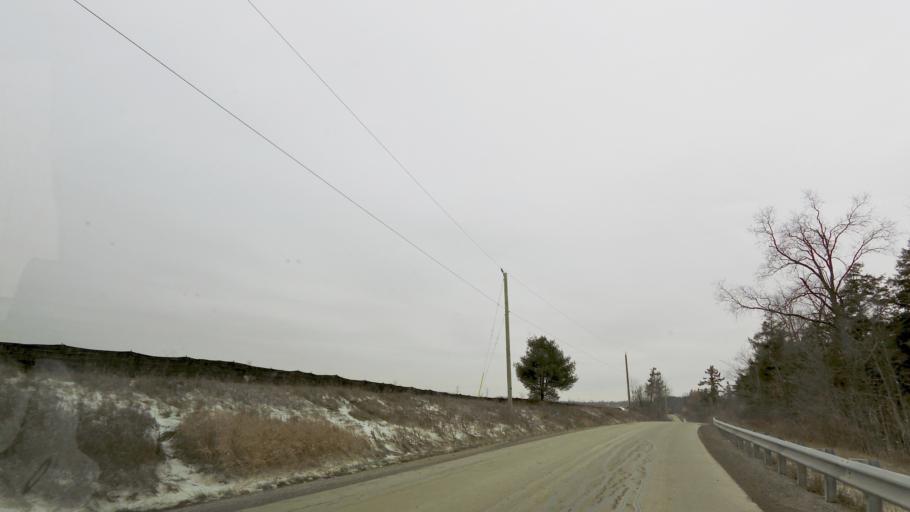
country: CA
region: Ontario
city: Vaughan
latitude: 43.8617
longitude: -79.6167
